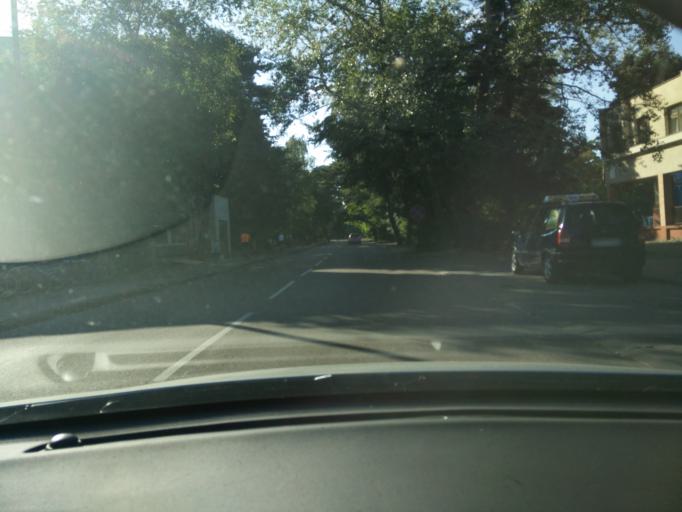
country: PL
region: Pomeranian Voivodeship
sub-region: Powiat pucki
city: Jastarnia
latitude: 54.6846
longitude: 18.7128
